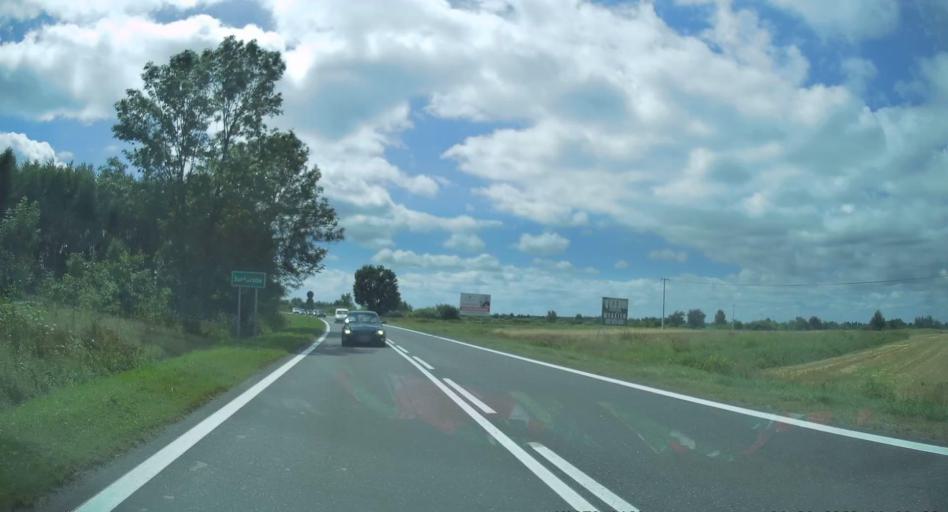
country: PL
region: Subcarpathian Voivodeship
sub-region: Powiat tarnobrzeski
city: Baranow Sandomierski
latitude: 50.5026
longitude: 21.5722
